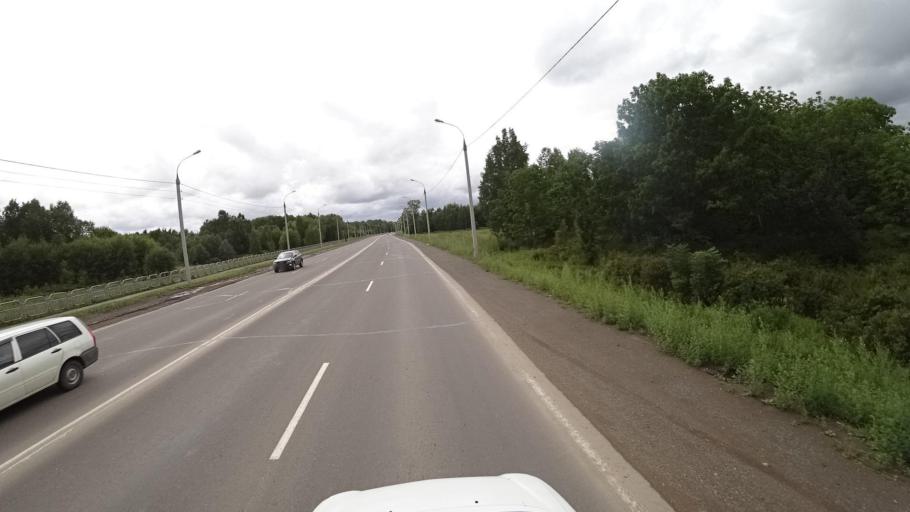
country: RU
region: Khabarovsk Krai
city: Solnechnyy
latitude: 50.5891
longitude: 137.0298
